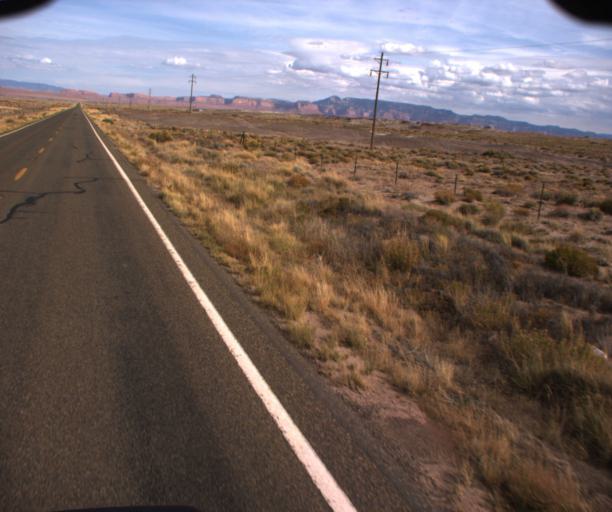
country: US
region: Arizona
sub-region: Apache County
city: Many Farms
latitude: 36.4723
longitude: -109.5205
